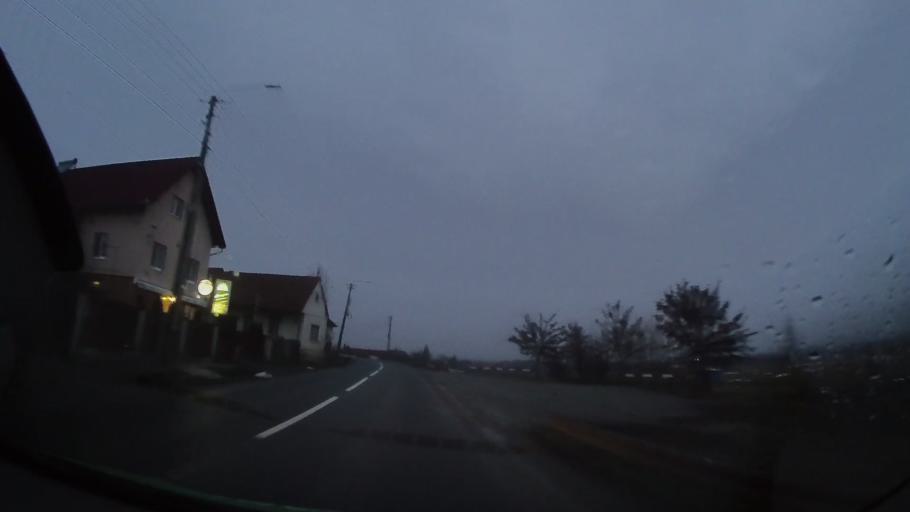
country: RO
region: Harghita
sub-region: Comuna Remetea
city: Remetea
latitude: 46.7953
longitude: 25.4561
